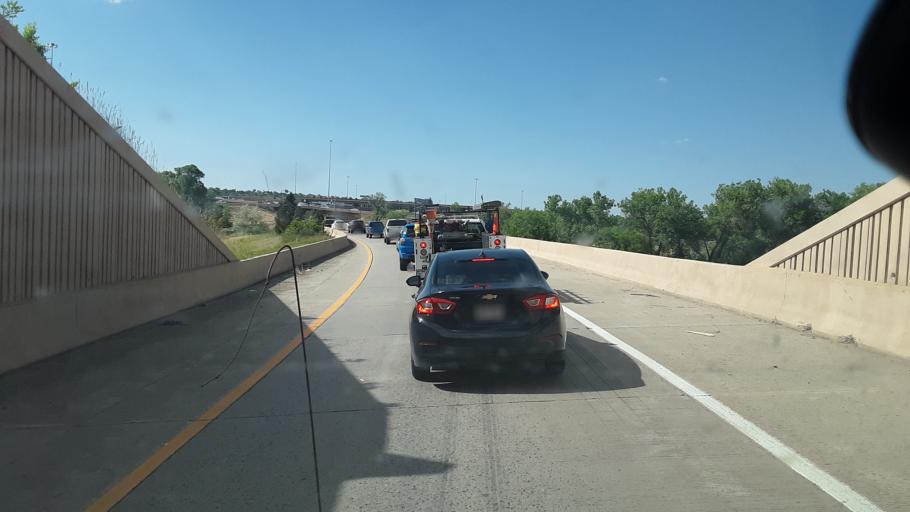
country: US
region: Colorado
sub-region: Adams County
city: Twin Lakes
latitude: 39.8205
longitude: -104.9803
